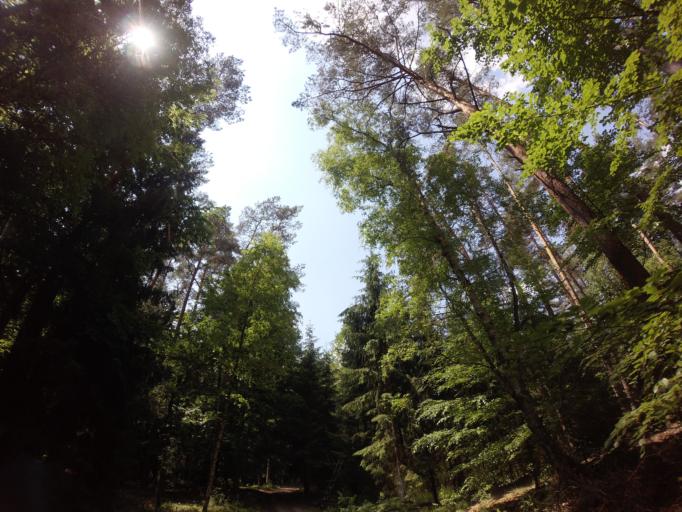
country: PL
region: West Pomeranian Voivodeship
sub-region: Powiat choszczenski
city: Bierzwnik
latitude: 53.0818
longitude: 15.7122
